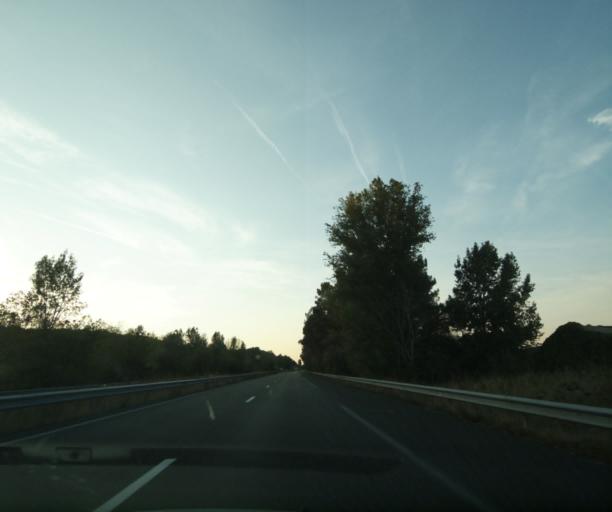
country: FR
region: Aquitaine
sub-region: Departement du Lot-et-Garonne
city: Buzet-sur-Baise
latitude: 44.2555
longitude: 0.2921
